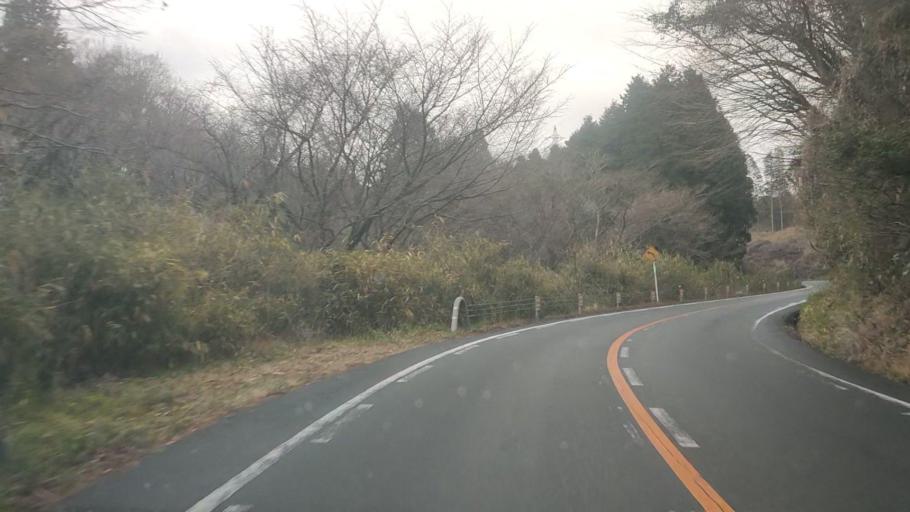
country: JP
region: Kumamoto
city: Aso
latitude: 32.8982
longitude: 130.9992
